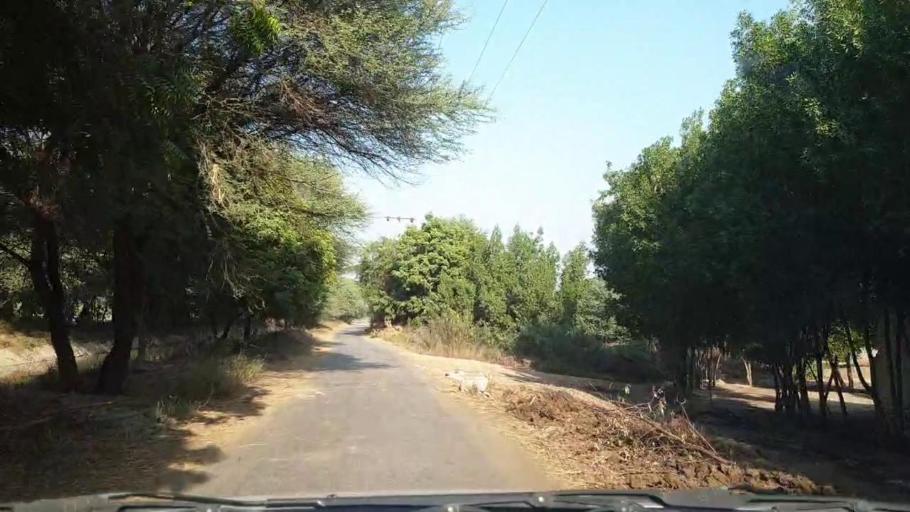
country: PK
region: Sindh
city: Tando Muhammad Khan
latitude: 25.2255
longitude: 68.6378
